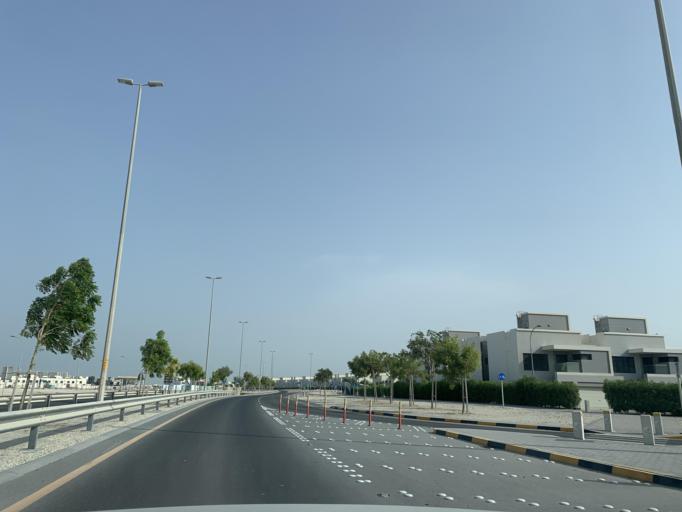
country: BH
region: Muharraq
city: Al Muharraq
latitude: 26.3179
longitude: 50.6312
